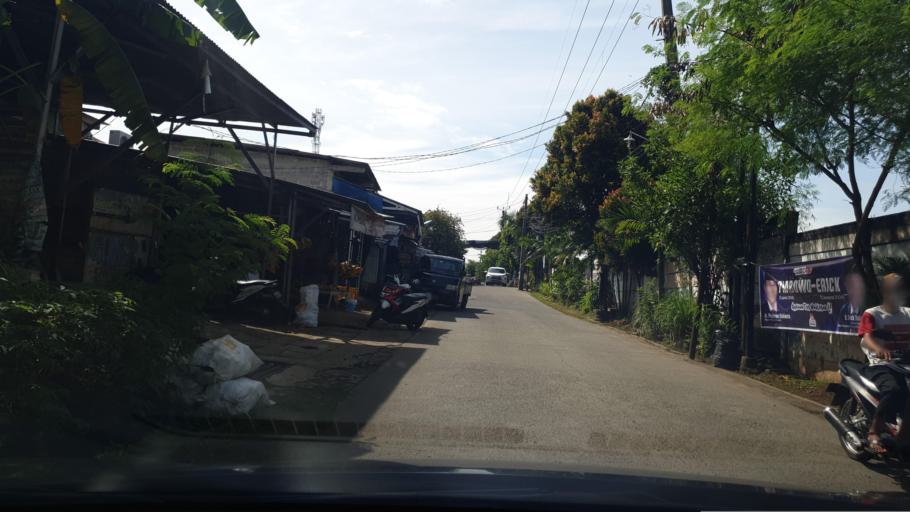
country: ID
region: West Java
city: Sawangan
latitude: -6.4090
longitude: 106.7791
